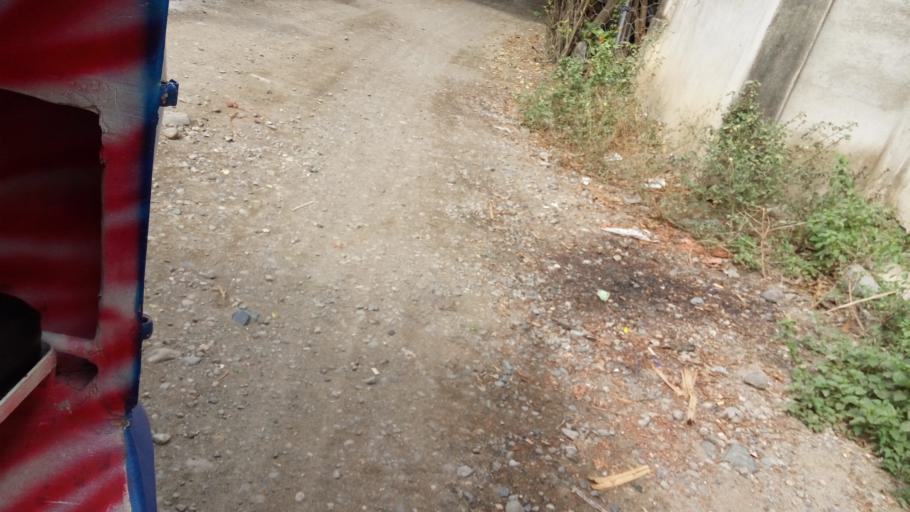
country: PH
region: Ilocos
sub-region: Province of La Union
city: Aringay
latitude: 16.3969
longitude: 120.3519
